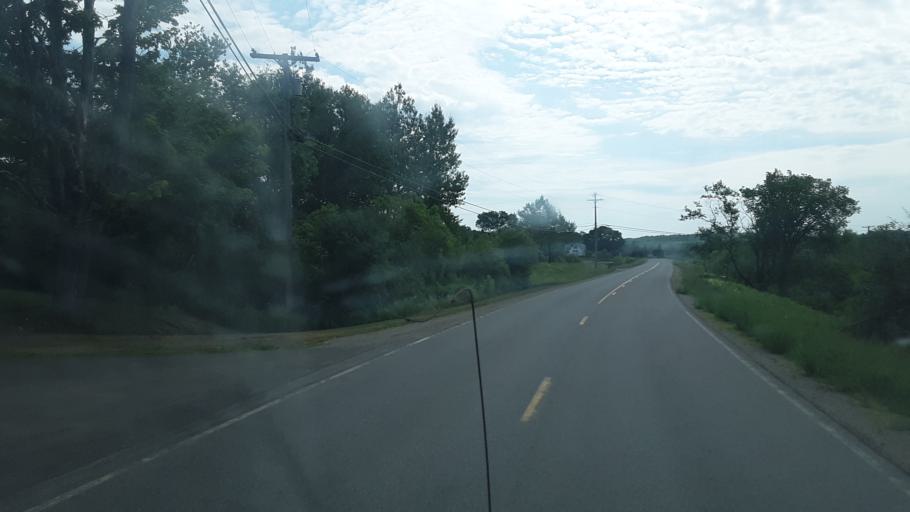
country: US
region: Maine
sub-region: Waldo County
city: Frankfort
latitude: 44.6144
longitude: -68.9298
